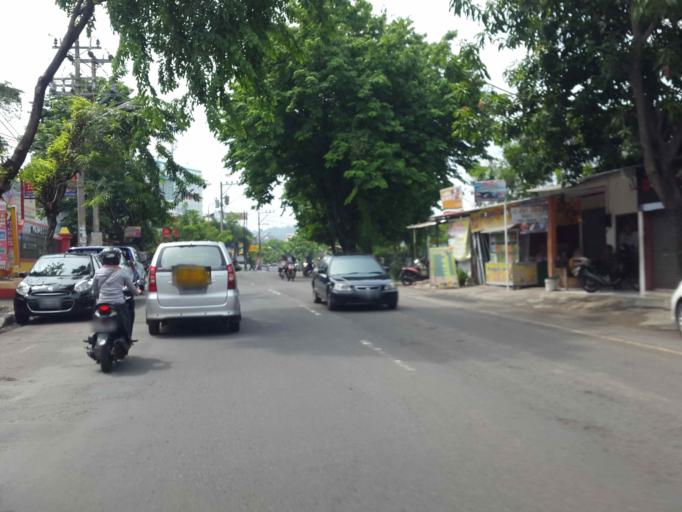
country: ID
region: Central Java
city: Semarang
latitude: -7.0063
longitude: 110.3962
